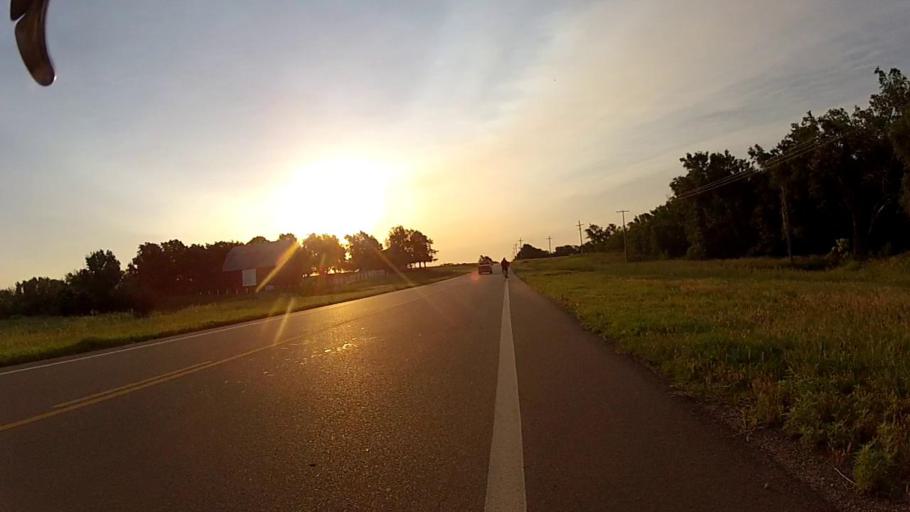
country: US
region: Kansas
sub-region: Harper County
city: Anthony
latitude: 37.1526
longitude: -97.9585
